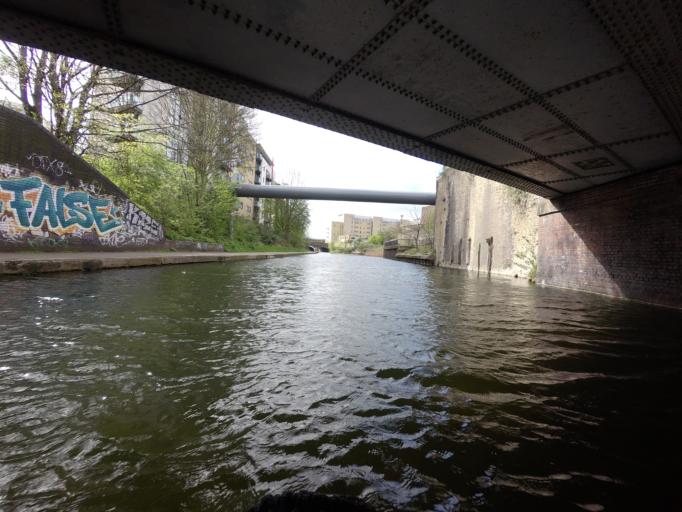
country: GB
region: England
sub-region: Greater London
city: Poplar
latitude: 51.5141
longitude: -0.0355
